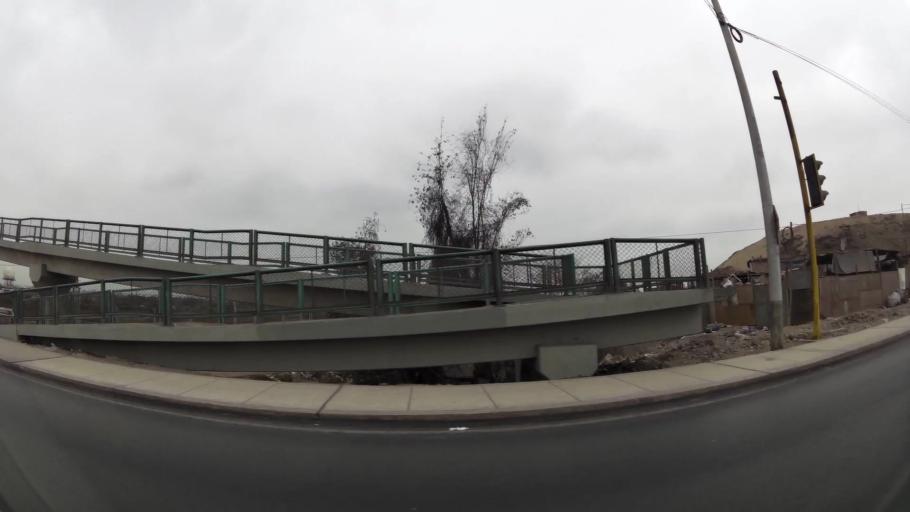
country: PE
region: Callao
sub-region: Callao
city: Callao
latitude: -12.0355
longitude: -77.1270
